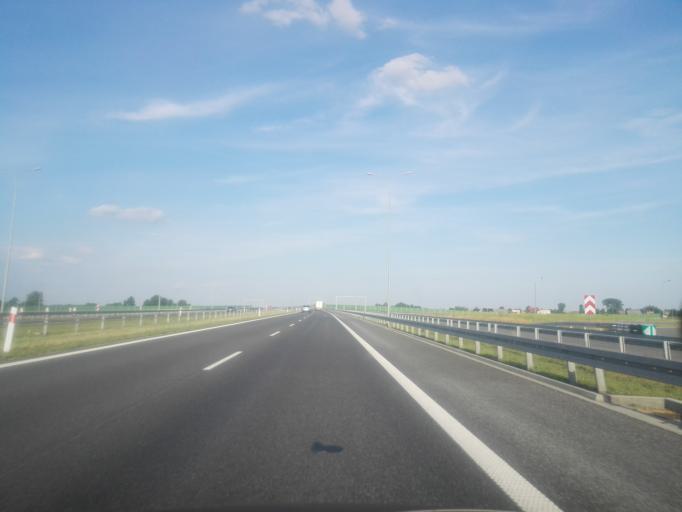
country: PL
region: Greater Poland Voivodeship
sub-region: Powiat kepinski
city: Kepno
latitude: 51.3159
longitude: 18.0046
